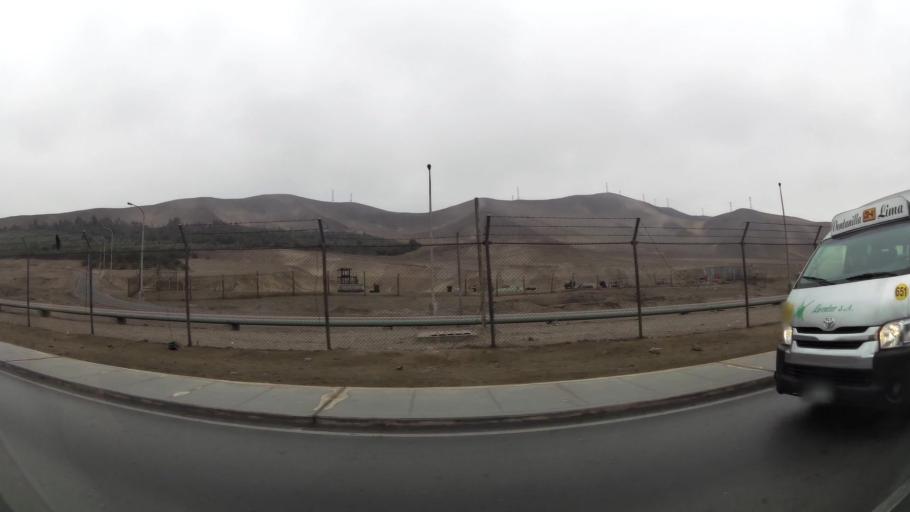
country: PE
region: Lima
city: Ventanilla
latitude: -11.9224
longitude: -77.1290
